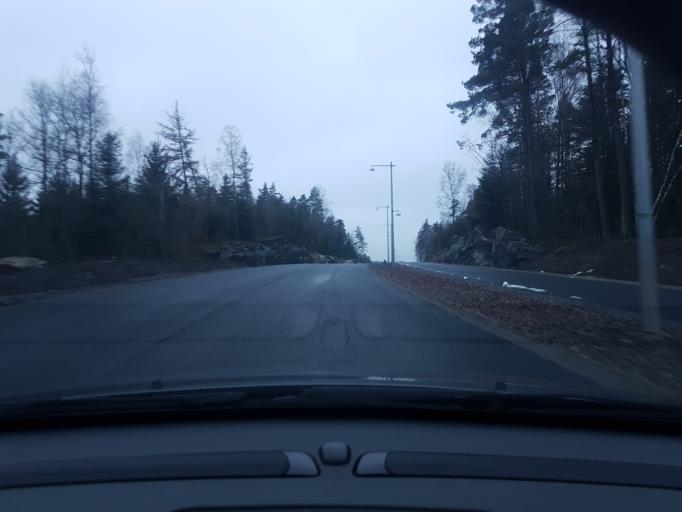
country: SE
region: Vaestra Goetaland
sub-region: Ale Kommun
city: Alvangen
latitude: 57.9477
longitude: 12.1304
